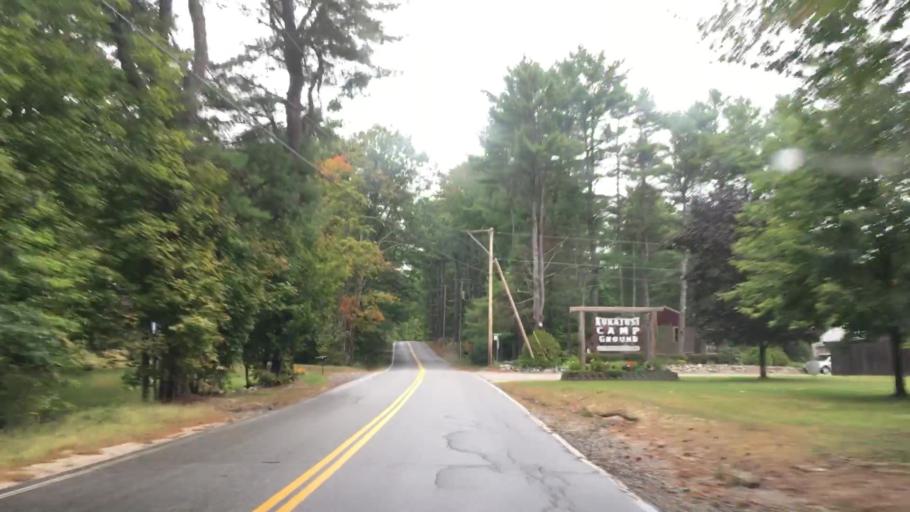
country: US
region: Maine
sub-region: Cumberland County
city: Raymond
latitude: 43.9587
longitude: -70.4648
